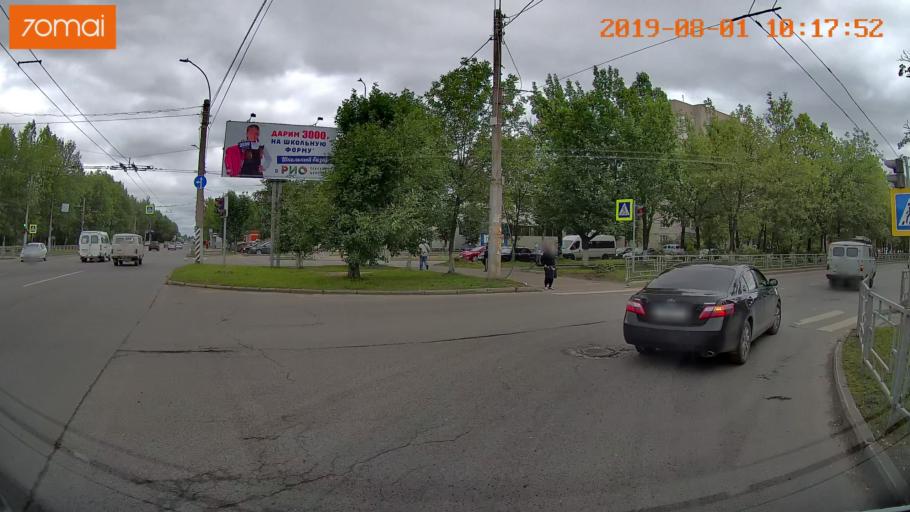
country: RU
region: Ivanovo
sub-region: Gorod Ivanovo
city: Ivanovo
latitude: 56.9646
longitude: 41.0022
